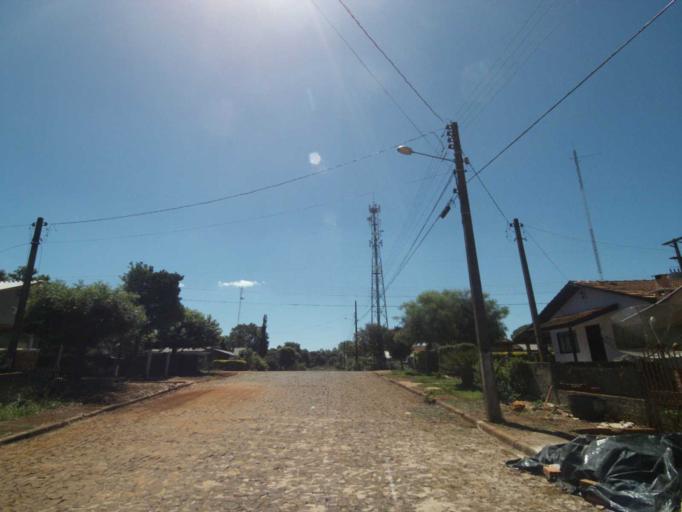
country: BR
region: Parana
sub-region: Laranjeiras Do Sul
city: Laranjeiras do Sul
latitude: -25.3887
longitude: -52.2145
